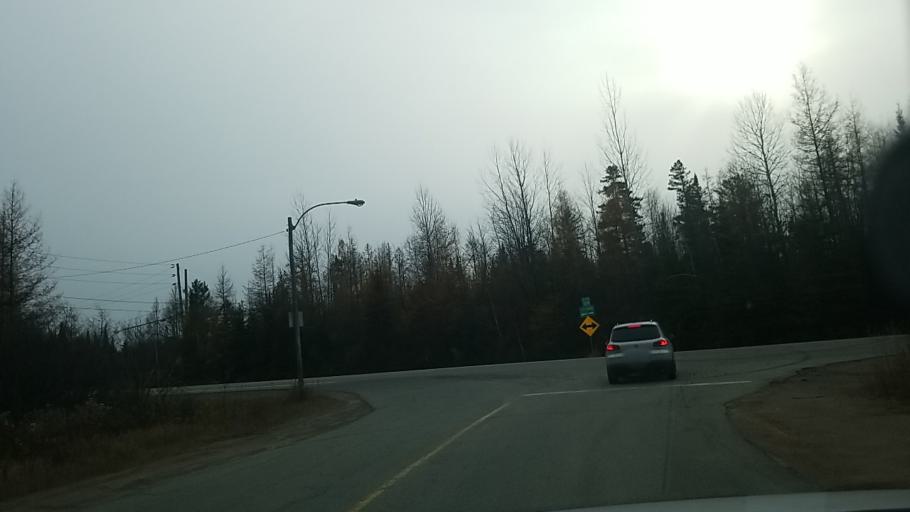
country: CA
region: Quebec
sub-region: Laurentides
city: Saint-Sauveur
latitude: 45.8170
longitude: -74.2493
